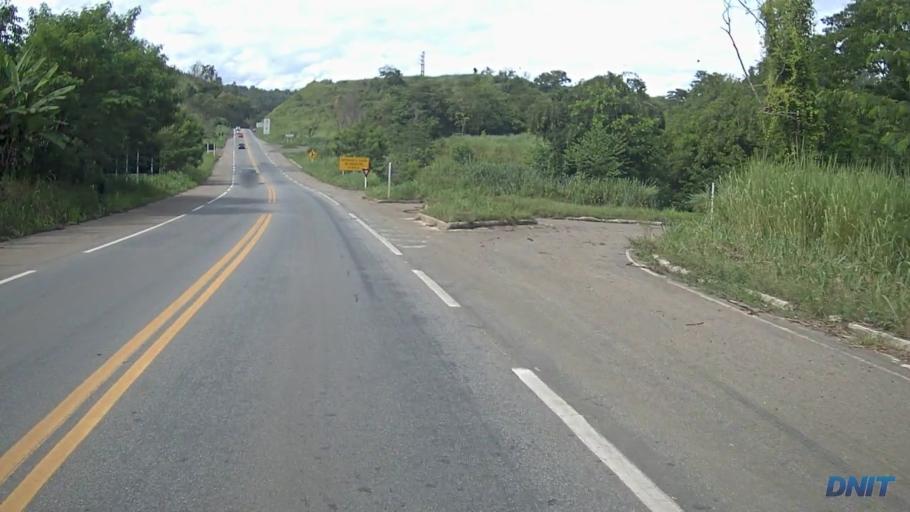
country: BR
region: Minas Gerais
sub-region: Ipaba
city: Ipaba
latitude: -19.3372
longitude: -42.4259
